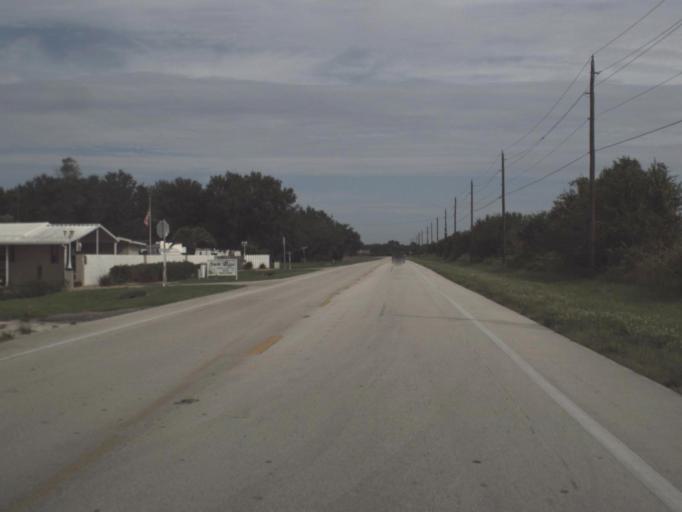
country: US
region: Florida
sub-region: DeSoto County
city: Southeast Arcadia
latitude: 27.1904
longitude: -81.8280
